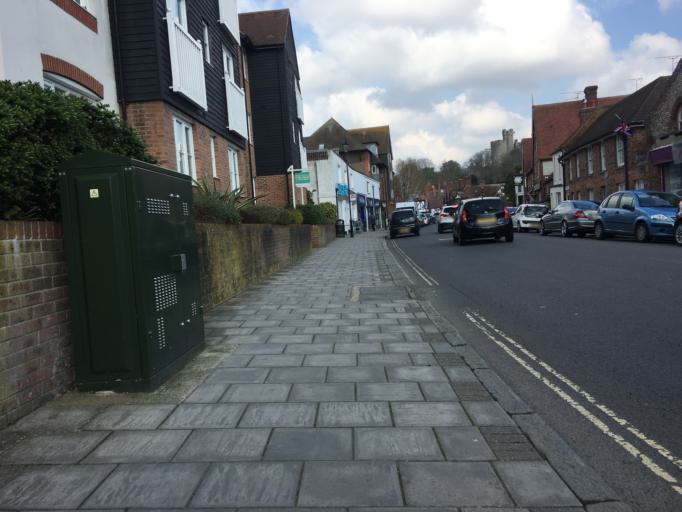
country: GB
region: England
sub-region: West Sussex
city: Arundel
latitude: 50.8526
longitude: -0.5519
